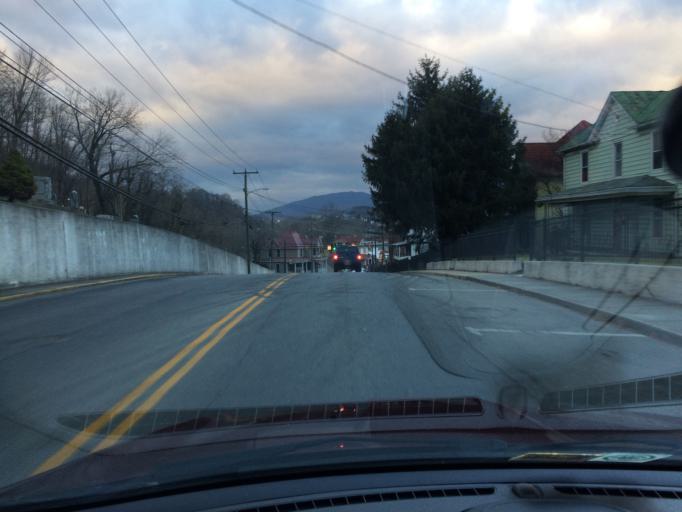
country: US
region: Virginia
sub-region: Alleghany County
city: Clifton Forge
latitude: 37.8154
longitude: -79.8174
